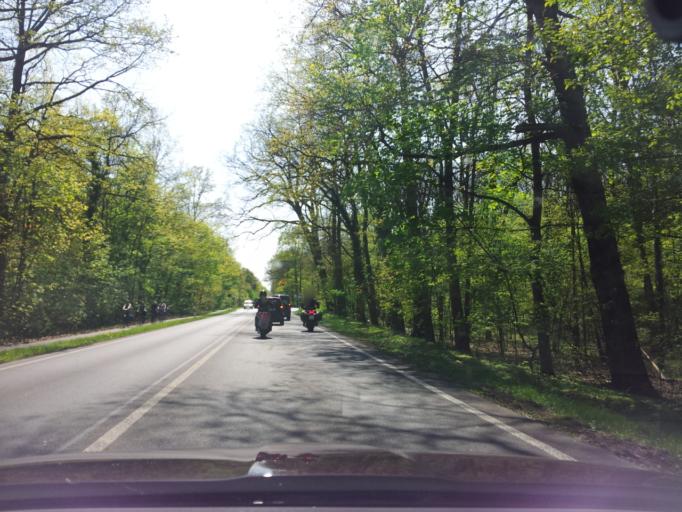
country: DE
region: Brandenburg
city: Michendorf
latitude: 52.2873
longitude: 13.0163
